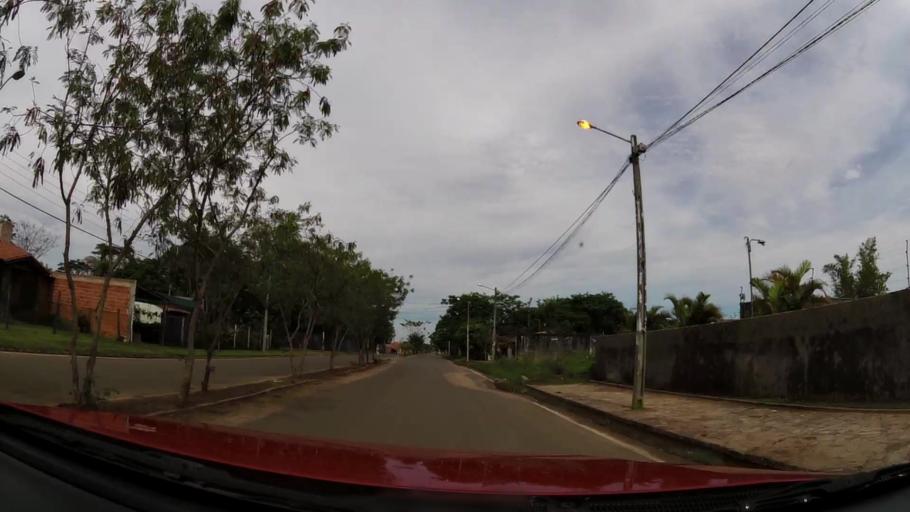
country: PY
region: Central
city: Limpio
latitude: -25.1748
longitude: -57.4751
